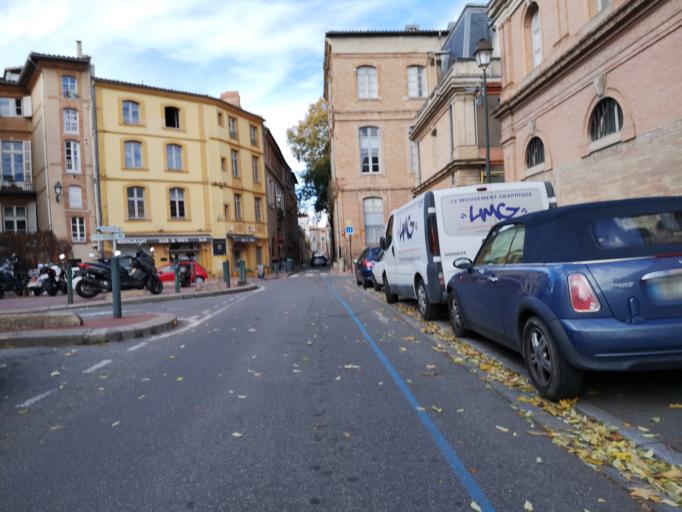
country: FR
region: Midi-Pyrenees
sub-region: Departement de la Haute-Garonne
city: Toulouse
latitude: 43.5967
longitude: 1.4504
